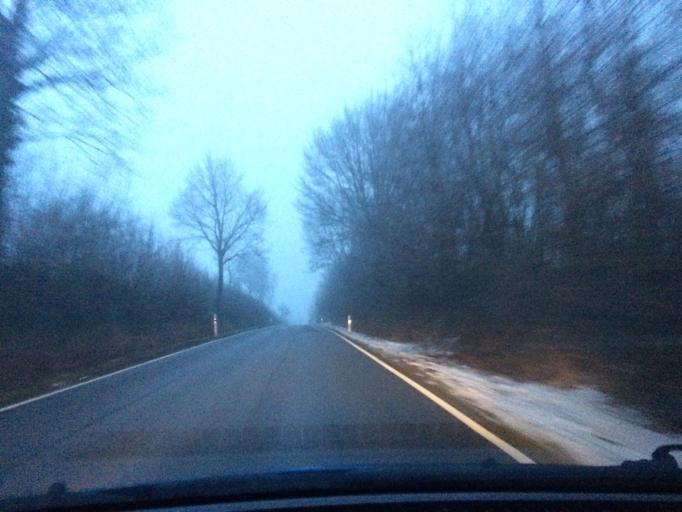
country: DE
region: Schleswig-Holstein
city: Kollow
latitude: 53.4546
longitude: 10.4577
